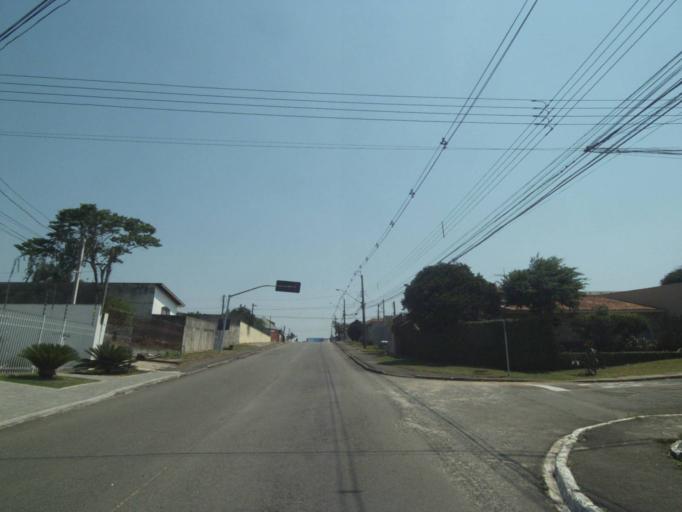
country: BR
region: Parana
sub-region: Sao Jose Dos Pinhais
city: Sao Jose dos Pinhais
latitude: -25.5080
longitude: -49.2714
